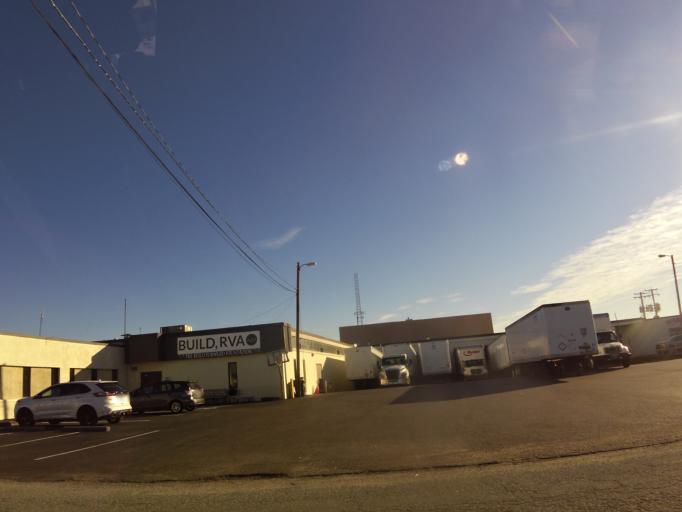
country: US
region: Virginia
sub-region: City of Richmond
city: Richmond
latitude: 37.5767
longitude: -77.4698
